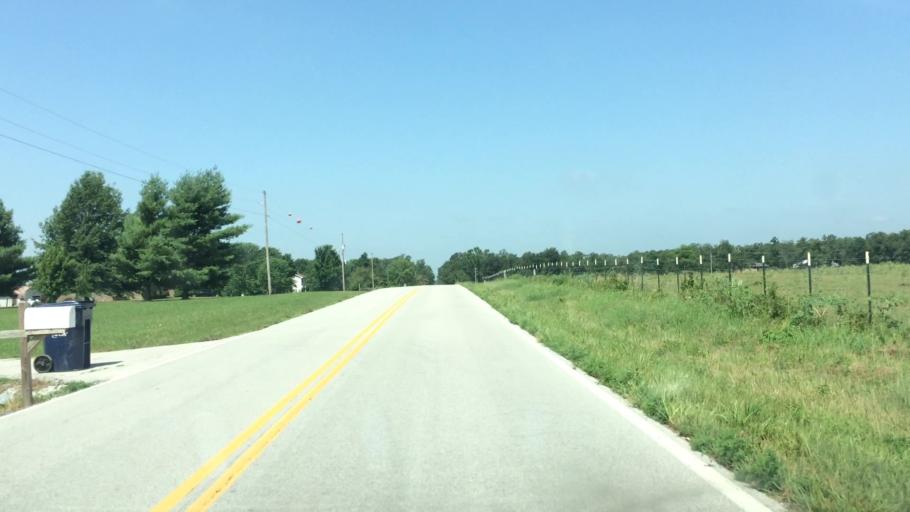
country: US
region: Missouri
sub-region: Greene County
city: Strafford
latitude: 37.2717
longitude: -93.1715
